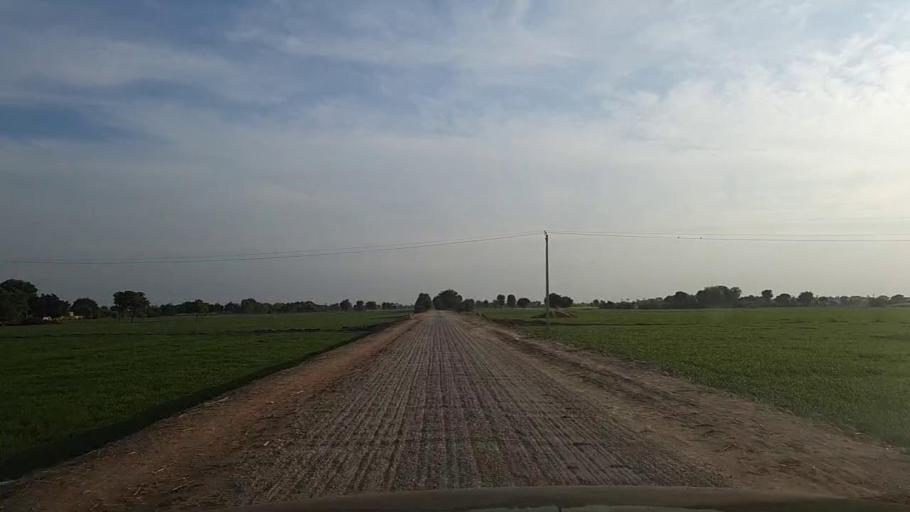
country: PK
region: Sindh
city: Jam Sahib
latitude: 26.4430
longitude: 68.5717
